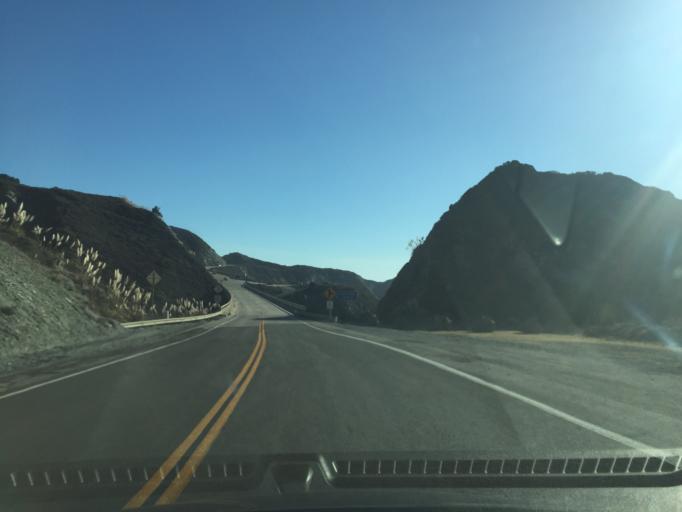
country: US
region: California
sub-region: Monterey County
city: King City
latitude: 35.8952
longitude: -121.4602
